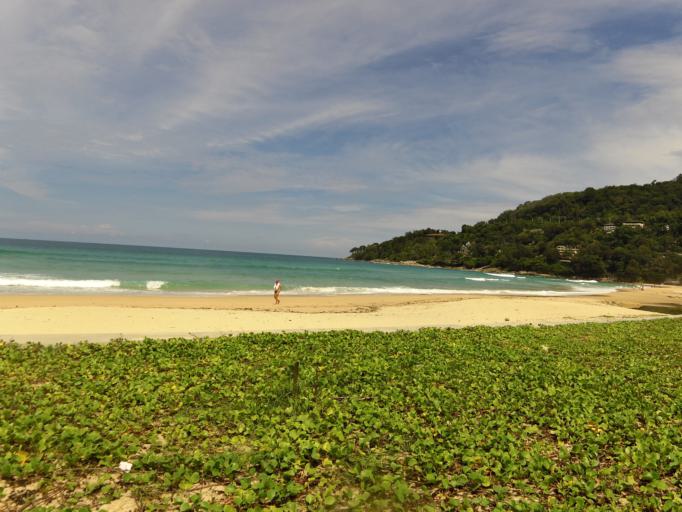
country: TH
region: Phuket
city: Ban Karon
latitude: 7.8549
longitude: 98.2913
